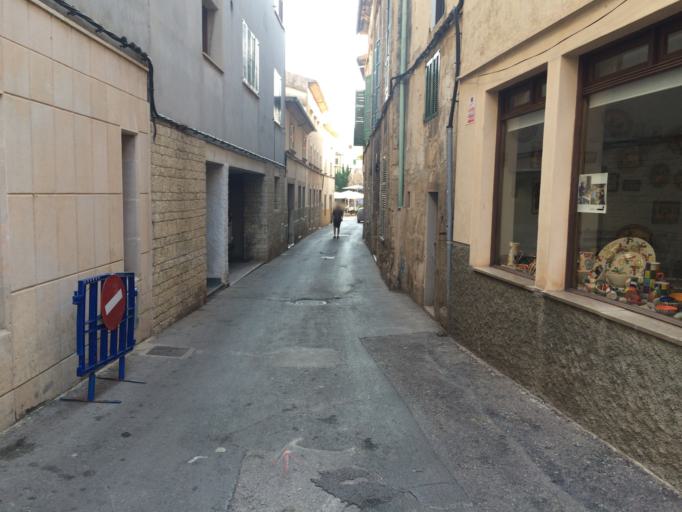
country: ES
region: Balearic Islands
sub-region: Illes Balears
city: Pollenca
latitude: 39.8782
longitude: 3.0156
